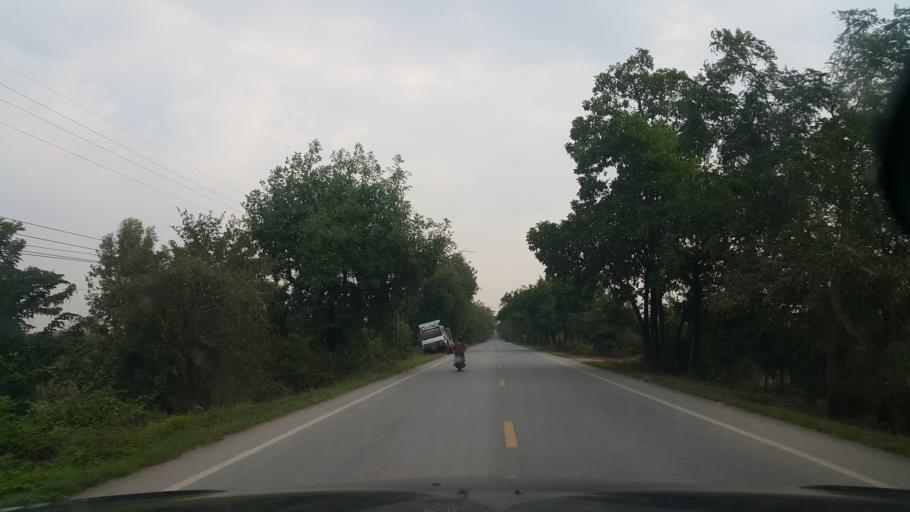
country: TH
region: Sukhothai
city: Si Samrong
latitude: 17.1696
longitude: 99.7153
